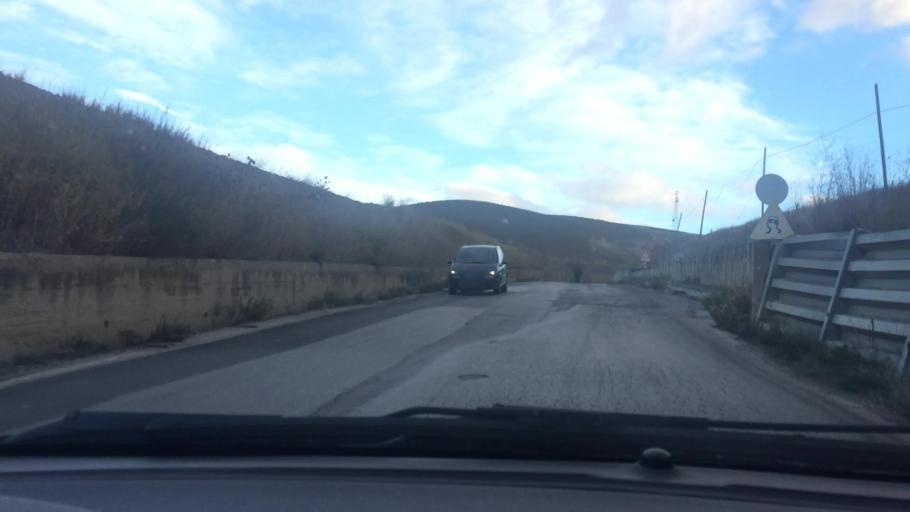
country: IT
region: Basilicate
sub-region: Provincia di Potenza
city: Tolve
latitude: 40.7038
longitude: 16.0145
